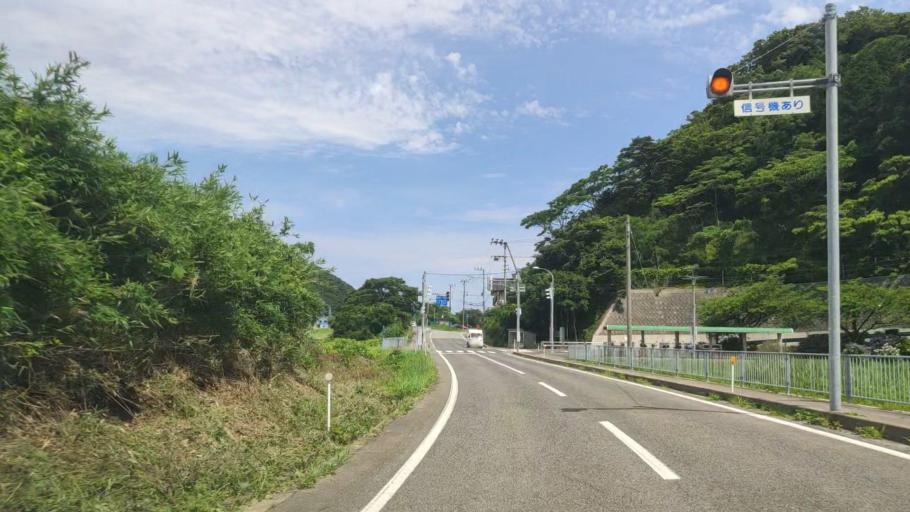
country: JP
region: Hyogo
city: Toyooka
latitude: 35.6517
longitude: 134.7634
